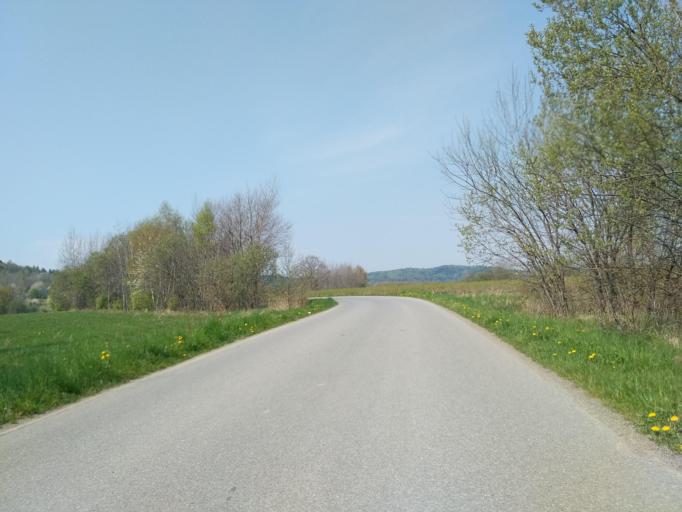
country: PL
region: Subcarpathian Voivodeship
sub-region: Powiat krosnienski
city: Chorkowka
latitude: 49.6238
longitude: 21.7232
